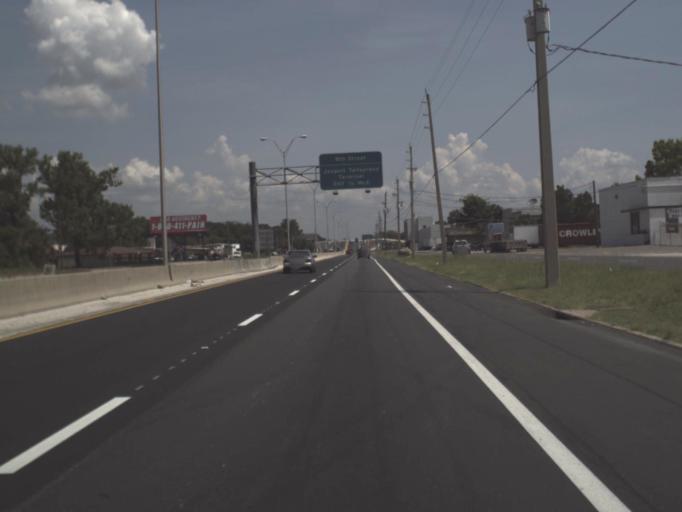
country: US
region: Florida
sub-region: Duval County
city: Jacksonville
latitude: 30.3373
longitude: -81.6366
